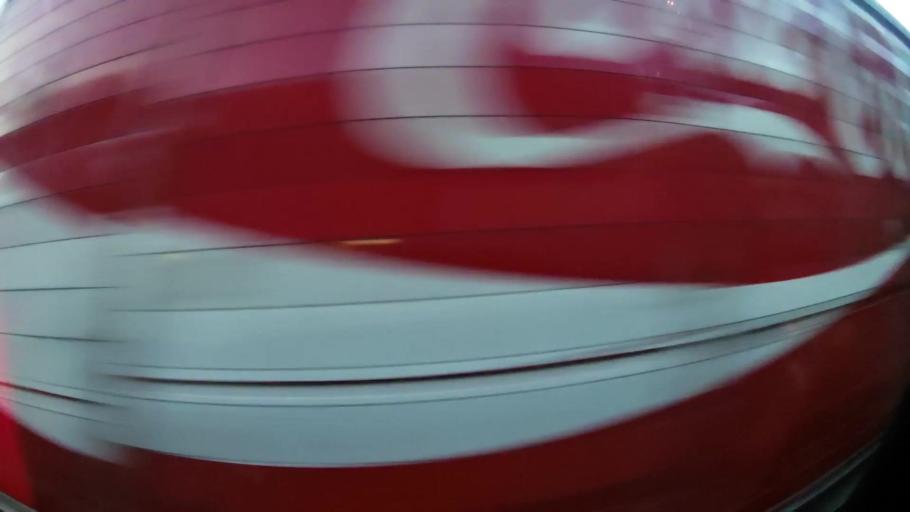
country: CO
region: Bogota D.C.
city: Barrio San Luis
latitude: 4.6570
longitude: -74.0680
